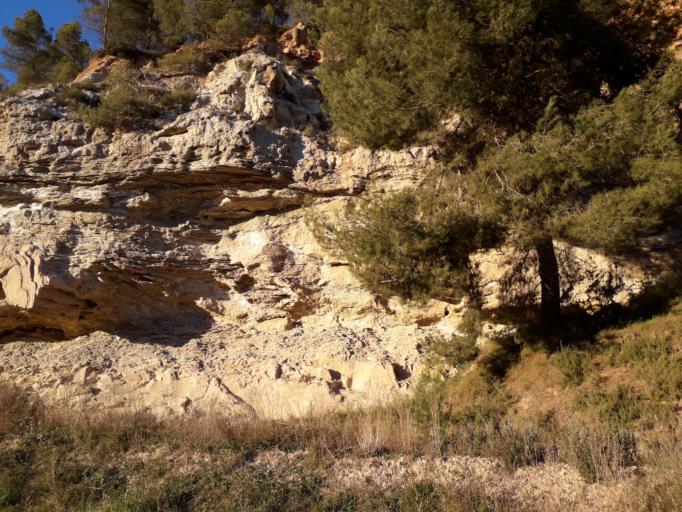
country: ES
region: Catalonia
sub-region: Provincia de Barcelona
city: Jorba
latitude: 41.5875
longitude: 1.5724
